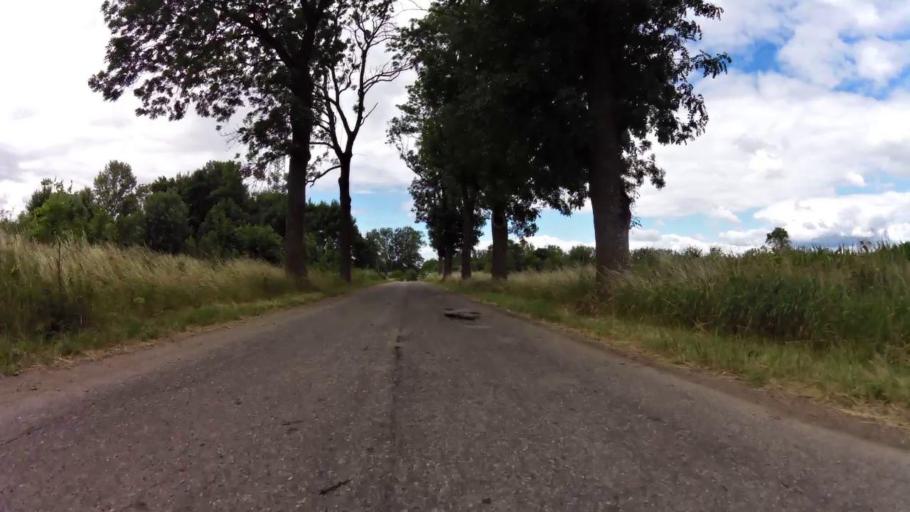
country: PL
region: West Pomeranian Voivodeship
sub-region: Powiat lobeski
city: Radowo Male
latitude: 53.7612
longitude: 15.5438
